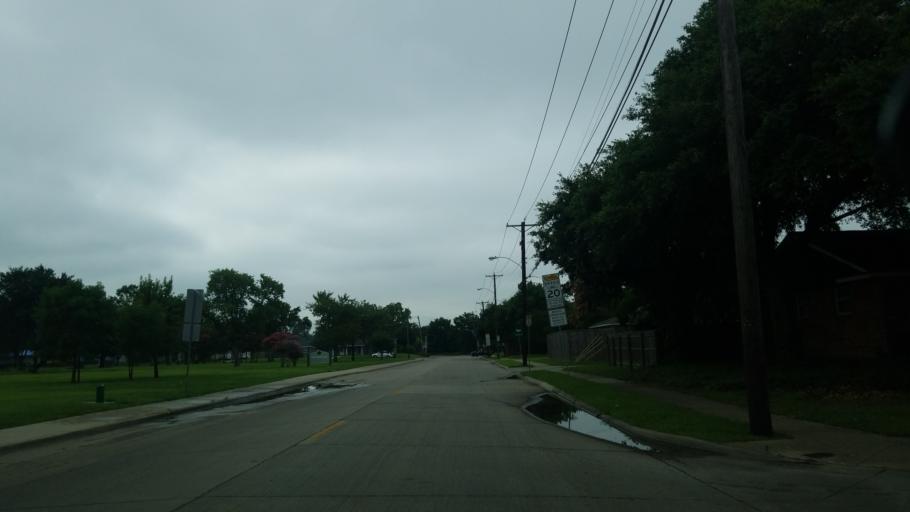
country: US
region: Texas
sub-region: Dallas County
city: Farmers Branch
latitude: 32.9046
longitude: -96.8640
